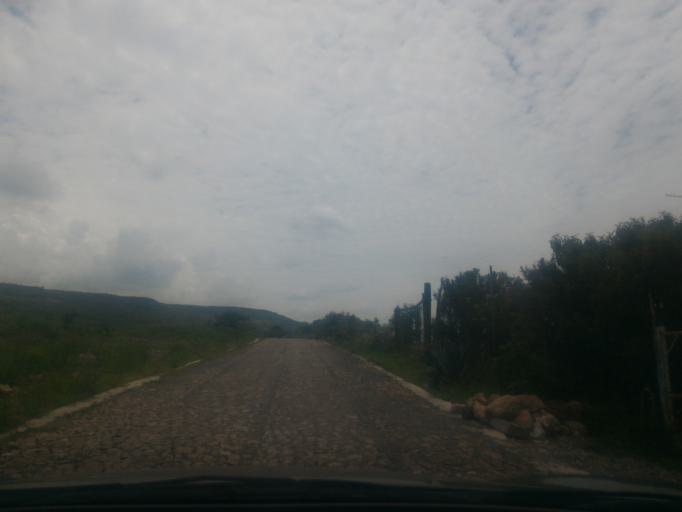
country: MX
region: Guanajuato
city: Ciudad Manuel Doblado
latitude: 20.7983
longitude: -102.0837
